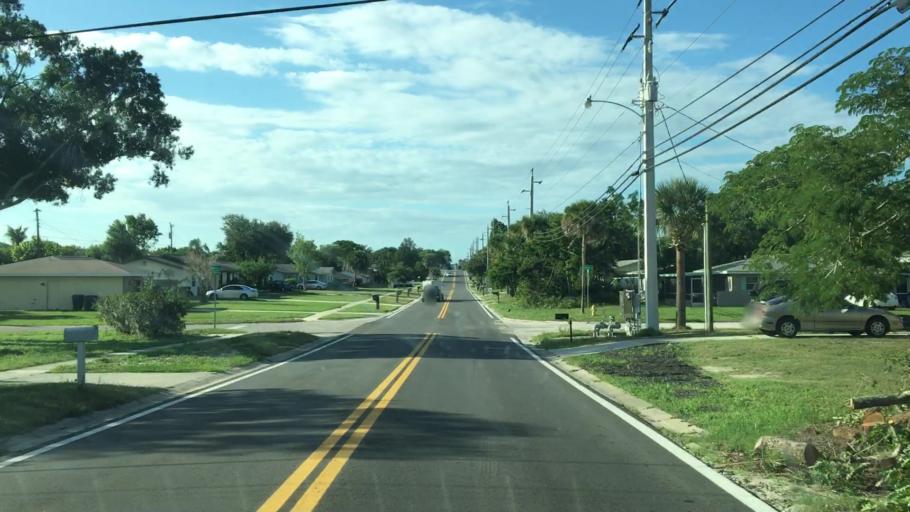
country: US
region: Florida
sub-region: Brevard County
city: Mims
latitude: 28.6261
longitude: -80.8604
